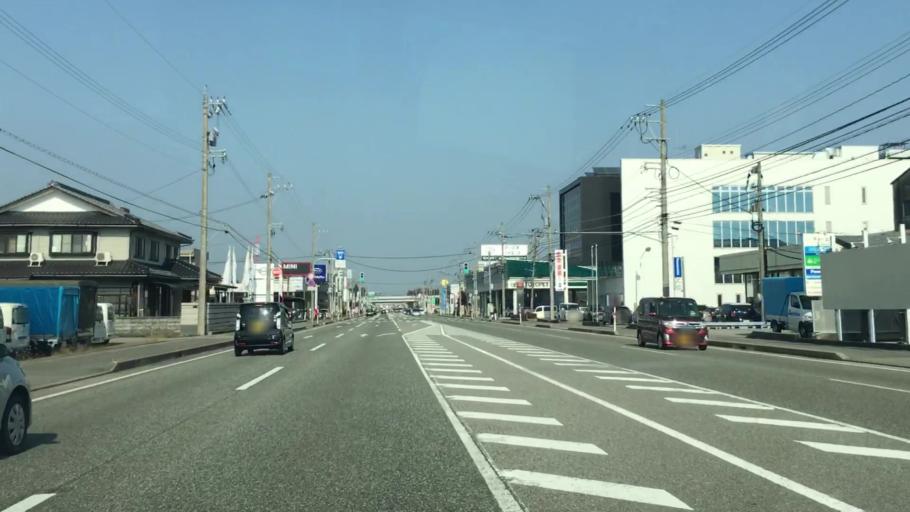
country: JP
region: Toyama
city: Toyama-shi
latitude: 36.6482
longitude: 137.2096
